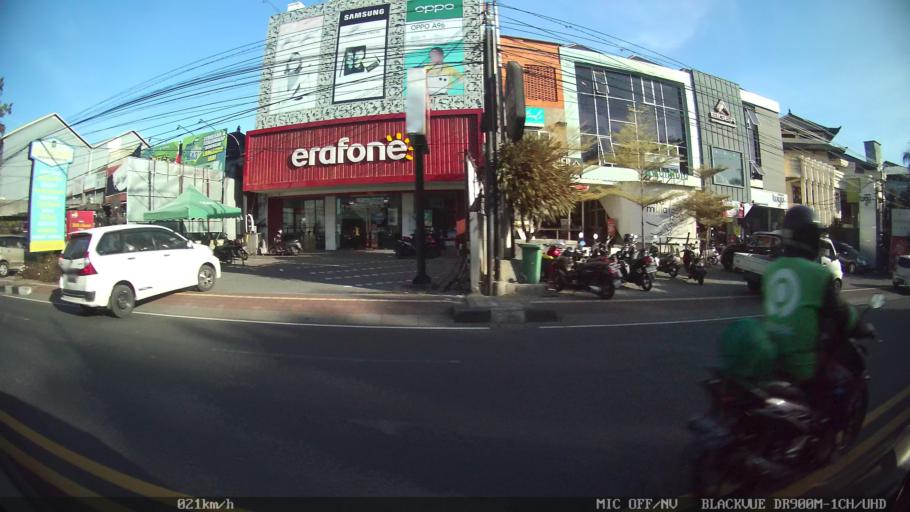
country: ID
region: Bali
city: Denpasar
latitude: -8.6365
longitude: 115.2166
